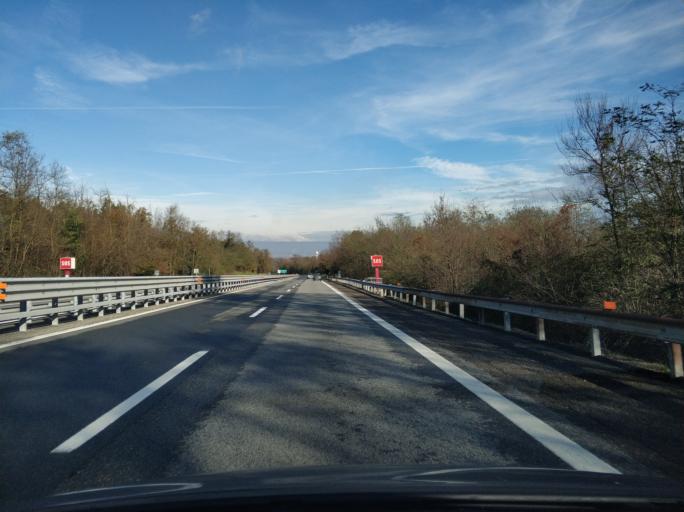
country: IT
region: Piedmont
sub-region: Provincia di Torino
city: Scarmagno
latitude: 45.3695
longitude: 7.8405
